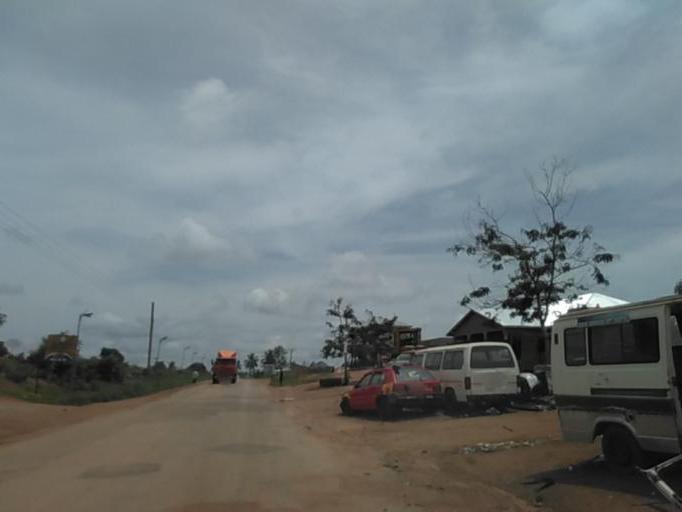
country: GH
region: Ashanti
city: Mamponteng
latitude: 6.8349
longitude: -1.5085
